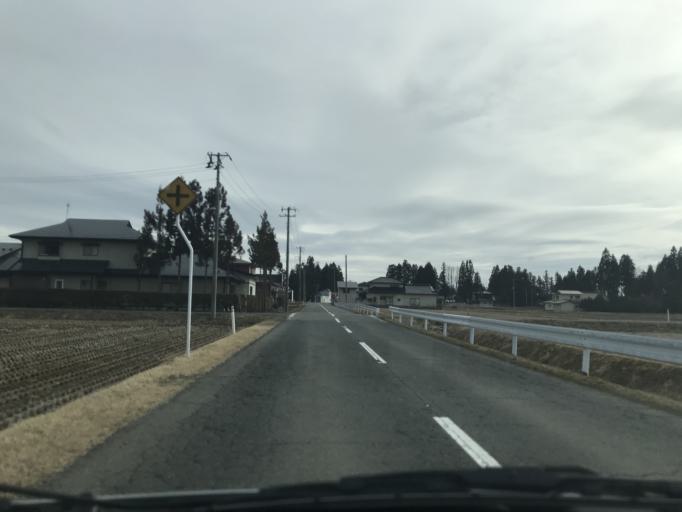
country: JP
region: Iwate
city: Hanamaki
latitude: 39.3678
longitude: 141.0687
